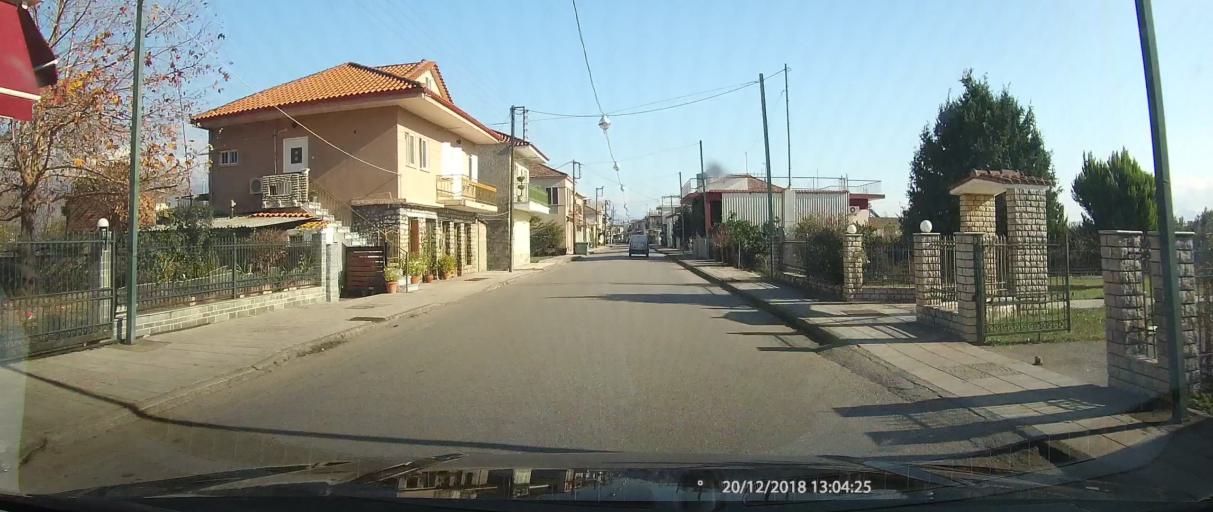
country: GR
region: West Greece
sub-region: Nomos Aitolias kai Akarnanias
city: Panaitolion
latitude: 38.5850
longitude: 21.4343
